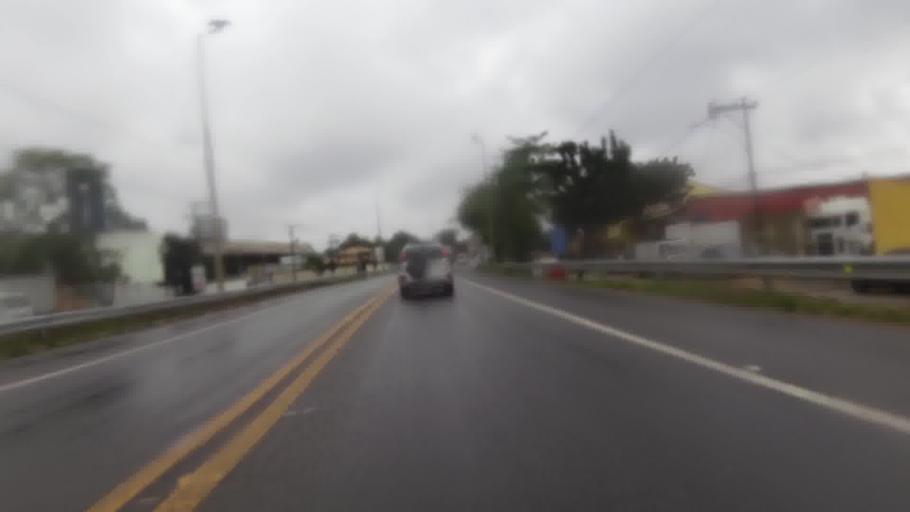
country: BR
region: Rio de Janeiro
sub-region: Campos Dos Goytacazes
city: Campos
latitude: -21.7141
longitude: -41.3088
